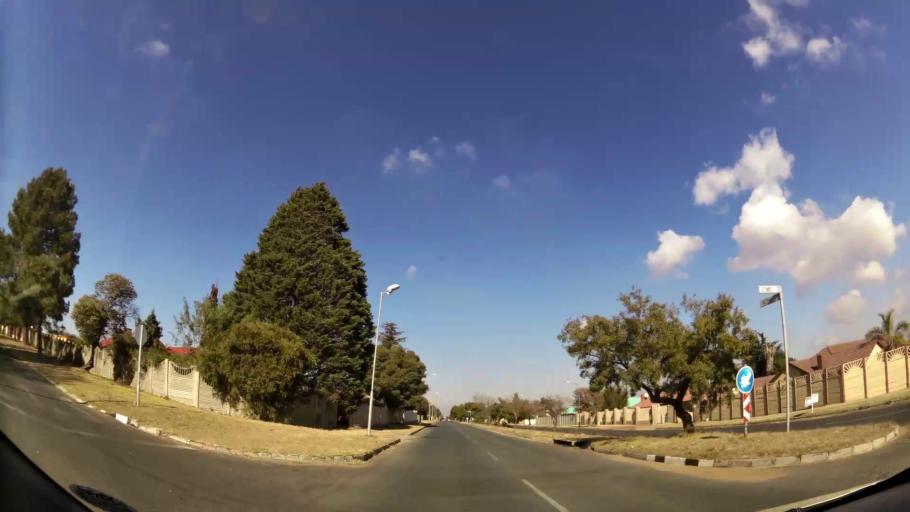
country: ZA
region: Gauteng
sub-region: City of Johannesburg Metropolitan Municipality
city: Roodepoort
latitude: -26.1440
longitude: 27.8259
